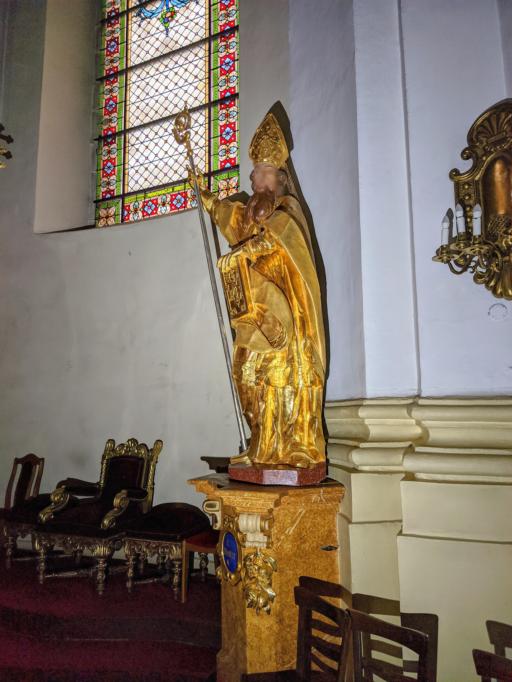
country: PL
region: Opole Voivodeship
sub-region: Powiat prudnicki
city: Prudnik
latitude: 50.3210
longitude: 17.5800
